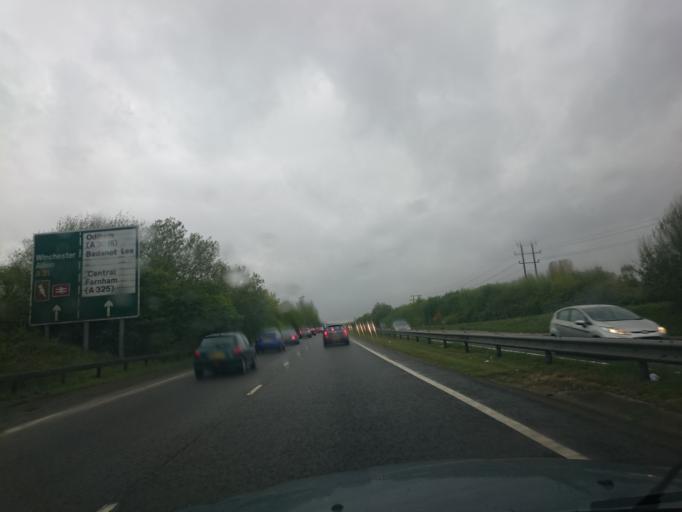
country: GB
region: England
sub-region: Hampshire
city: Aldershot
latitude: 51.2222
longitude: -0.7618
